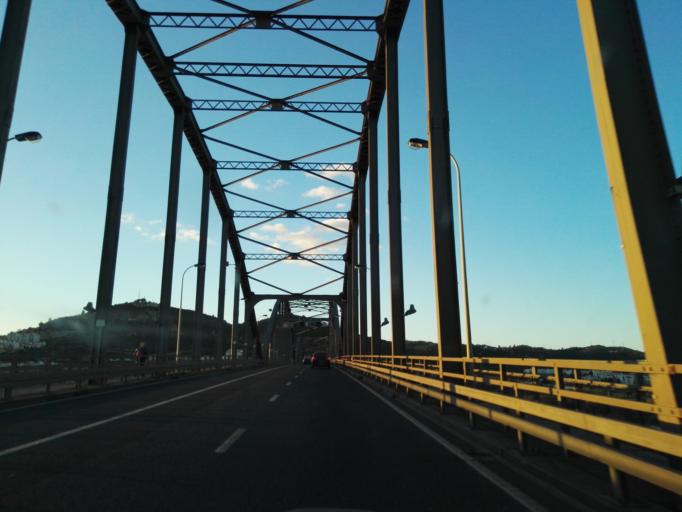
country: PT
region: Lisbon
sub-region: Vila Franca de Xira
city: Vila Franca de Xira
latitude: 38.9556
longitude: -8.9777
